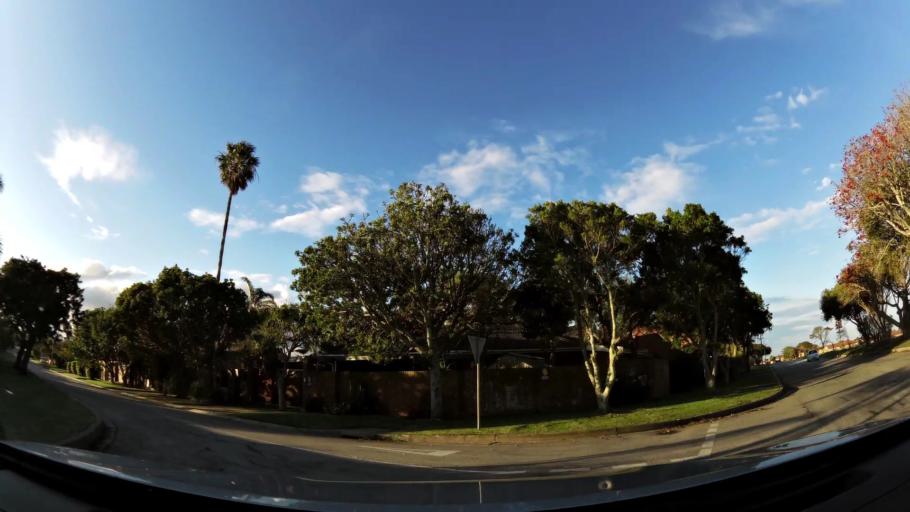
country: ZA
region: Eastern Cape
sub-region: Nelson Mandela Bay Metropolitan Municipality
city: Port Elizabeth
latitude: -33.9742
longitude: 25.4936
